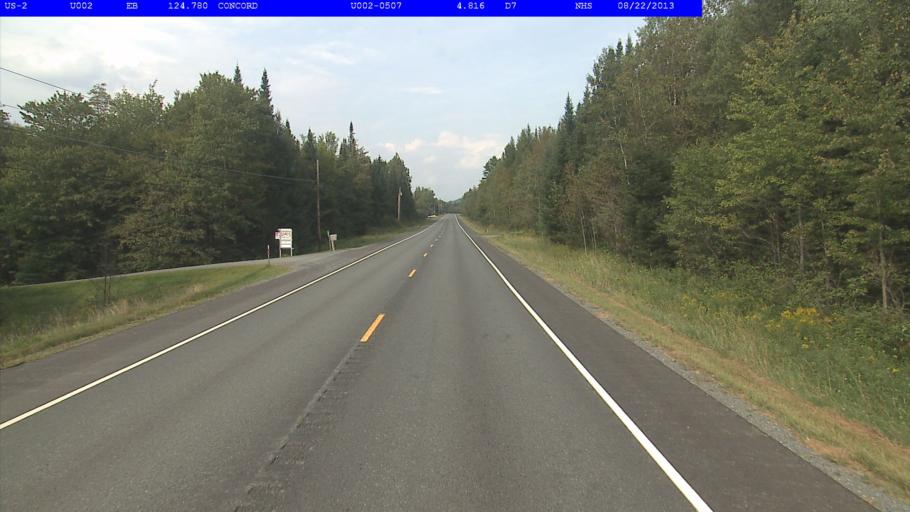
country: US
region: Vermont
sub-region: Caledonia County
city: St Johnsbury
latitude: 44.4609
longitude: -71.8633
